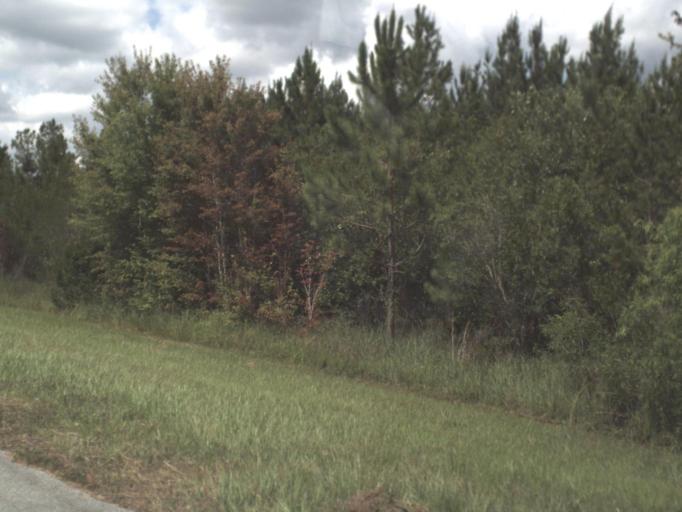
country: US
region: Florida
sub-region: Baker County
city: Macclenny
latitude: 30.2130
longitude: -82.1537
